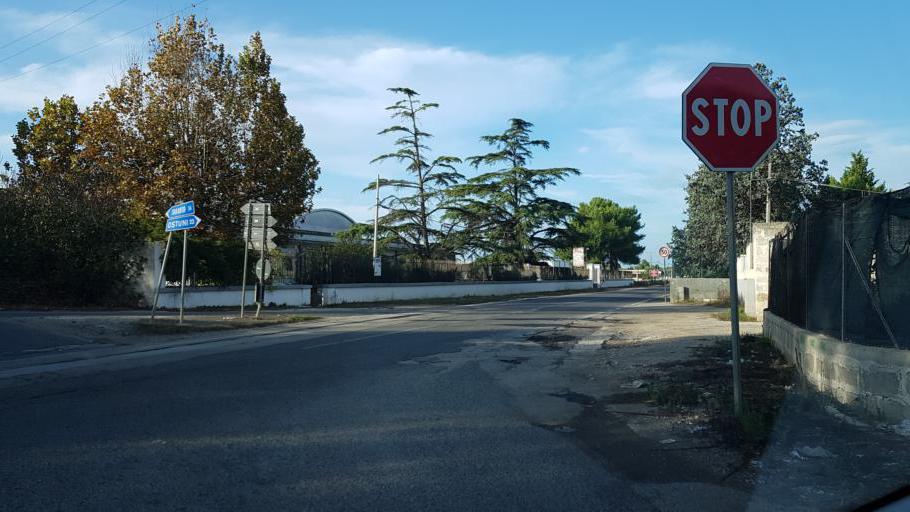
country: IT
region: Apulia
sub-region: Provincia di Brindisi
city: Francavilla Fontana
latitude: 40.5469
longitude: 17.5933
